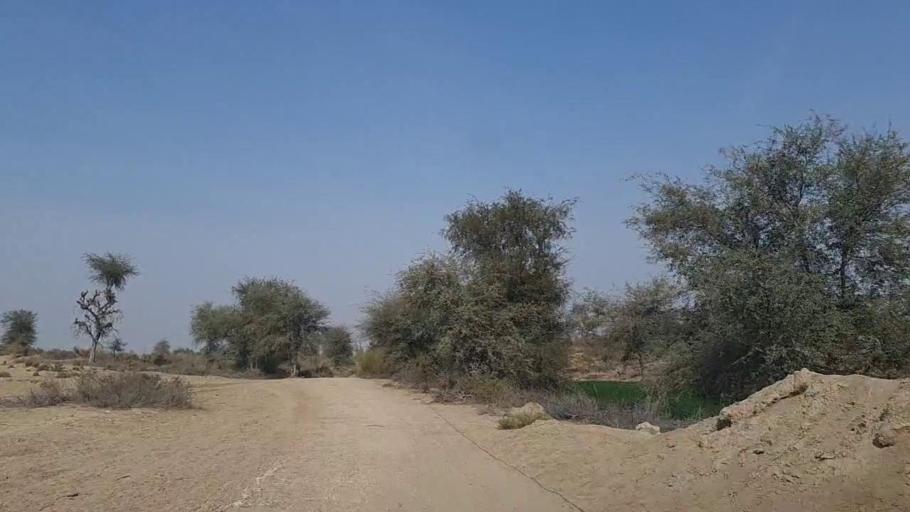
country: PK
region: Sindh
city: Daur
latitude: 26.5194
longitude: 68.4827
